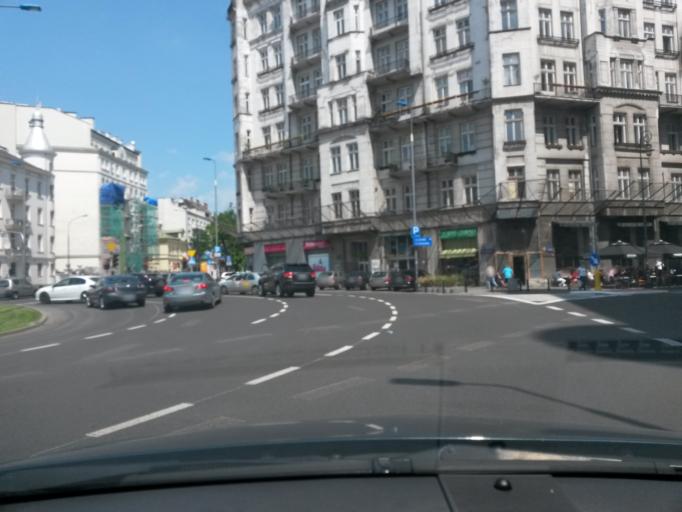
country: PL
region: Masovian Voivodeship
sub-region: Warszawa
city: Srodmiescie
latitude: 52.2134
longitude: 21.0220
